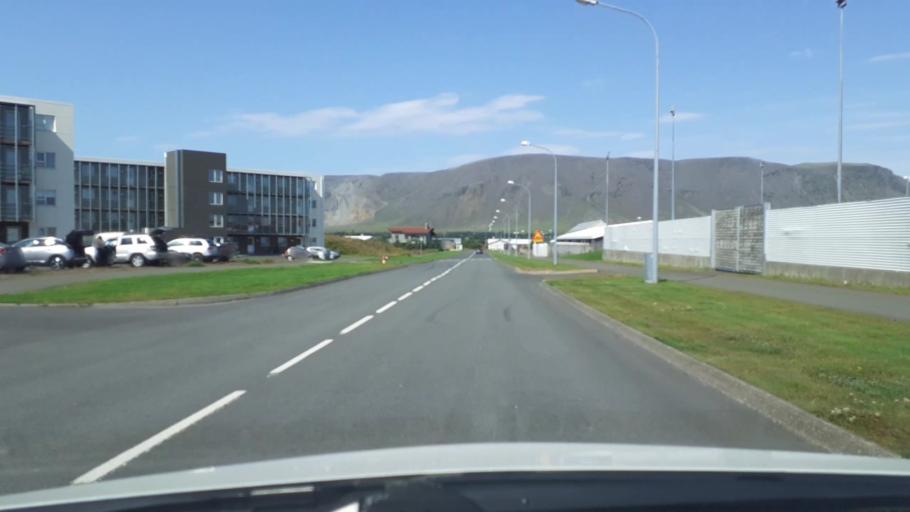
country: IS
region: South
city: Selfoss
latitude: 63.9314
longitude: -21.0187
